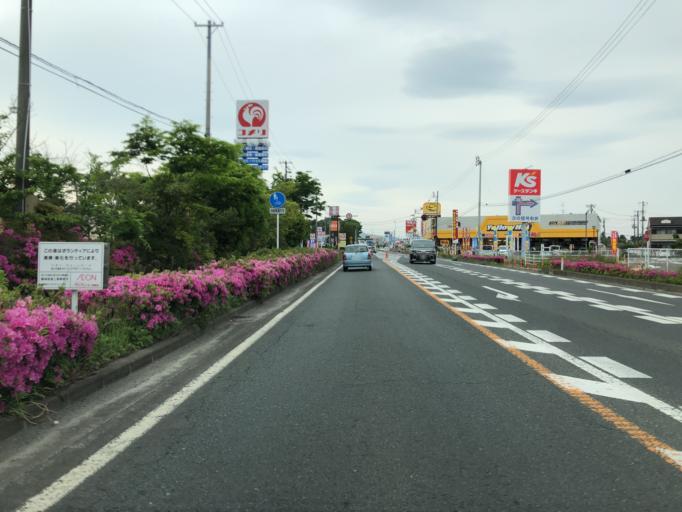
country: JP
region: Miyagi
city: Marumori
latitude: 37.7878
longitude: 140.9321
